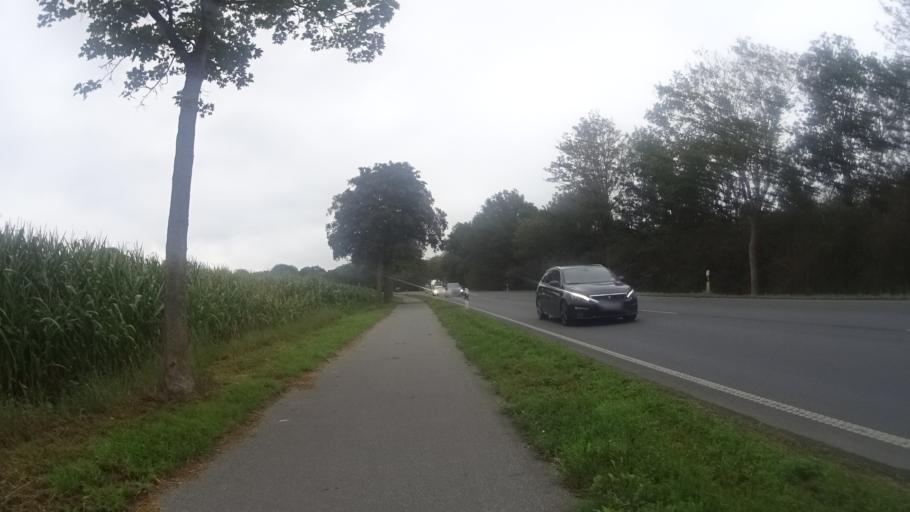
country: DE
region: North Rhine-Westphalia
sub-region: Regierungsbezirk Dusseldorf
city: Issum
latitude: 51.5250
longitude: 6.3939
